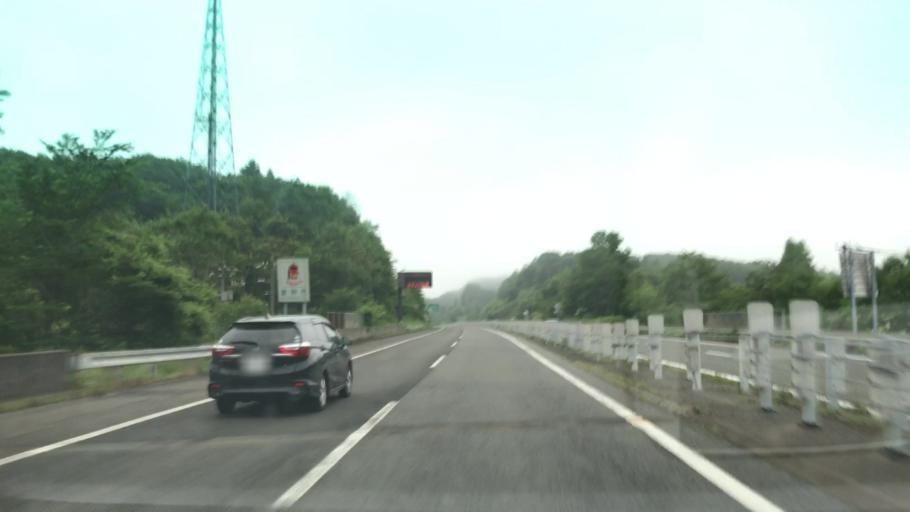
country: JP
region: Hokkaido
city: Shiraoi
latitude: 42.4647
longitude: 141.1812
